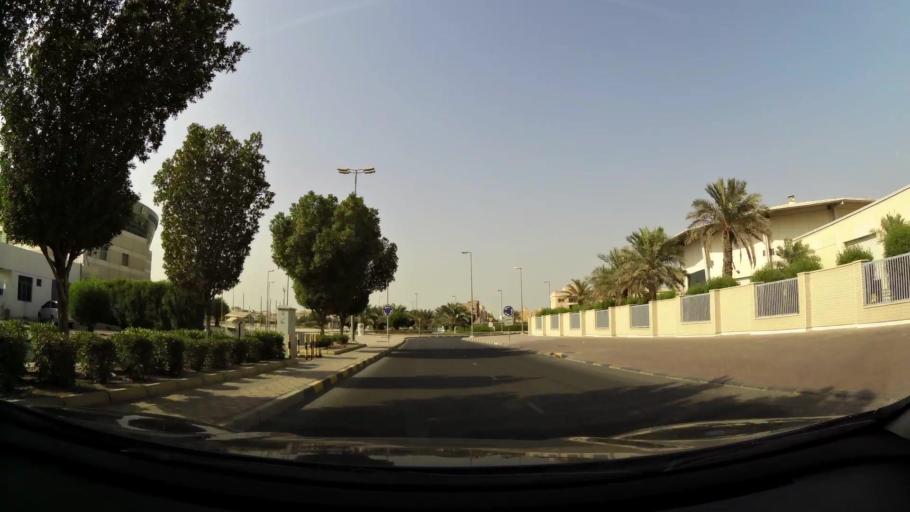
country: KW
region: Mubarak al Kabir
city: Sabah as Salim
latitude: 29.2749
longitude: 48.0489
